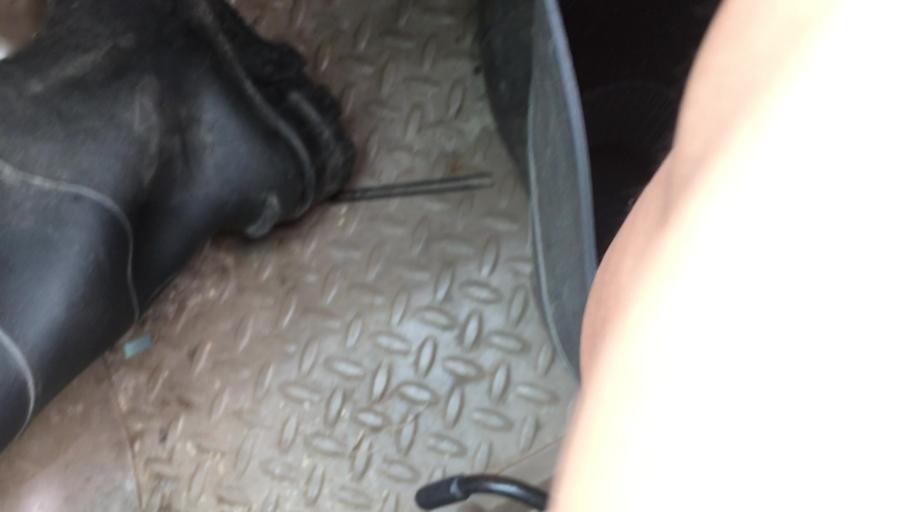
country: US
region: Maryland
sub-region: Worcester County
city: Pocomoke City
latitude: 38.0663
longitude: -75.5360
